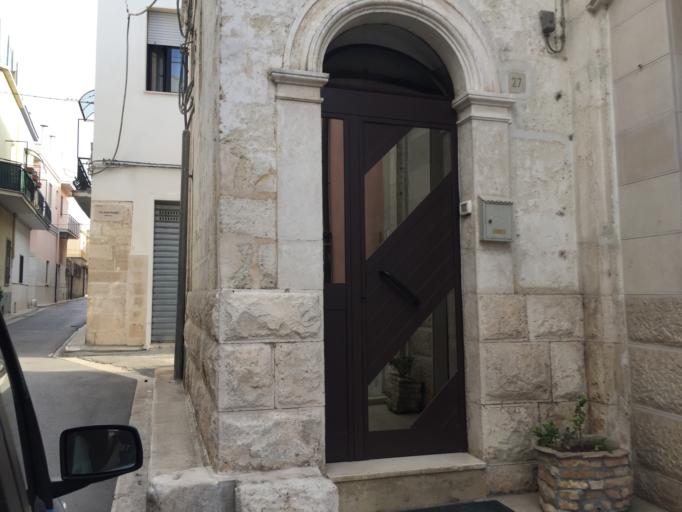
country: IT
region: Apulia
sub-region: Provincia di Bari
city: Capurso
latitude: 41.0465
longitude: 16.9207
